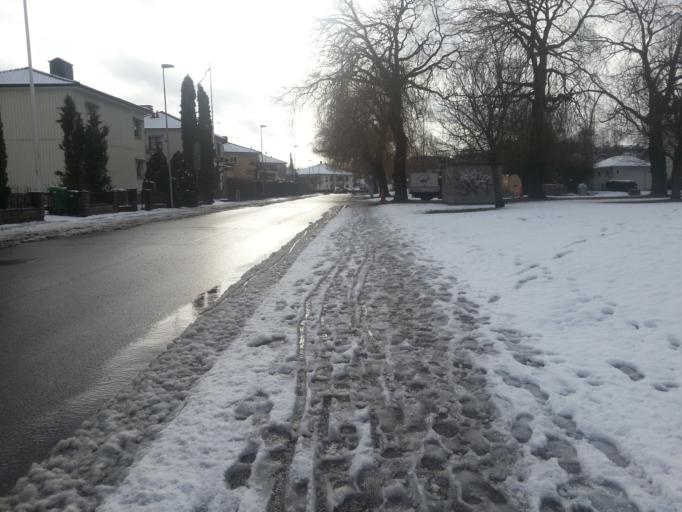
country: SE
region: OEstergoetland
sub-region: Norrkopings Kommun
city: Norrkoping
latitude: 58.5765
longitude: 16.1883
